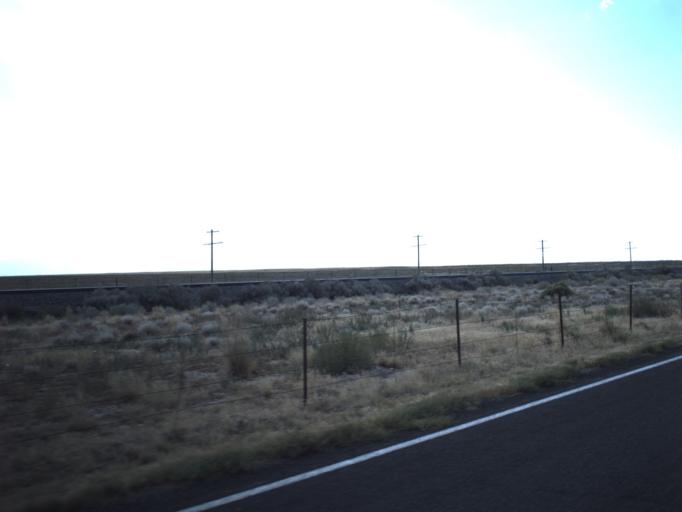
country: US
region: Utah
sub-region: Millard County
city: Delta
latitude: 38.9933
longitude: -112.7902
